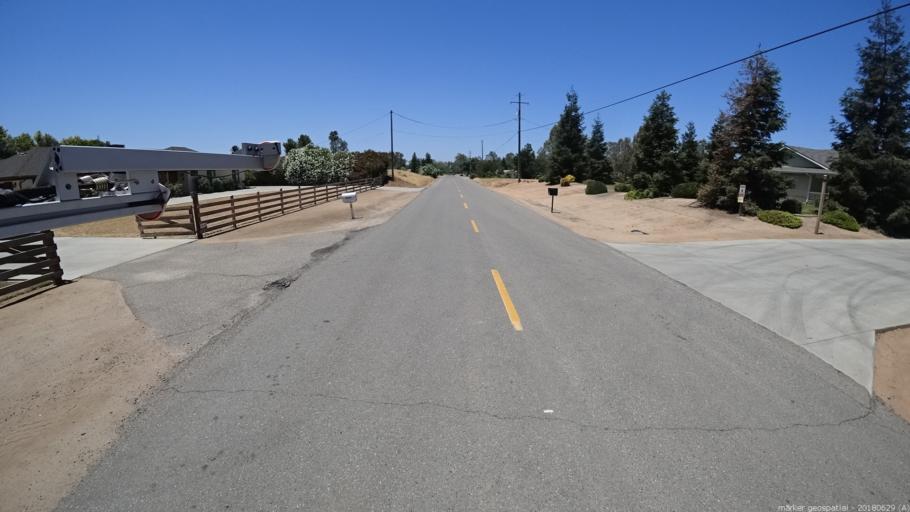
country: US
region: California
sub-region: Madera County
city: Parksdale
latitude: 36.9901
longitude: -119.9871
